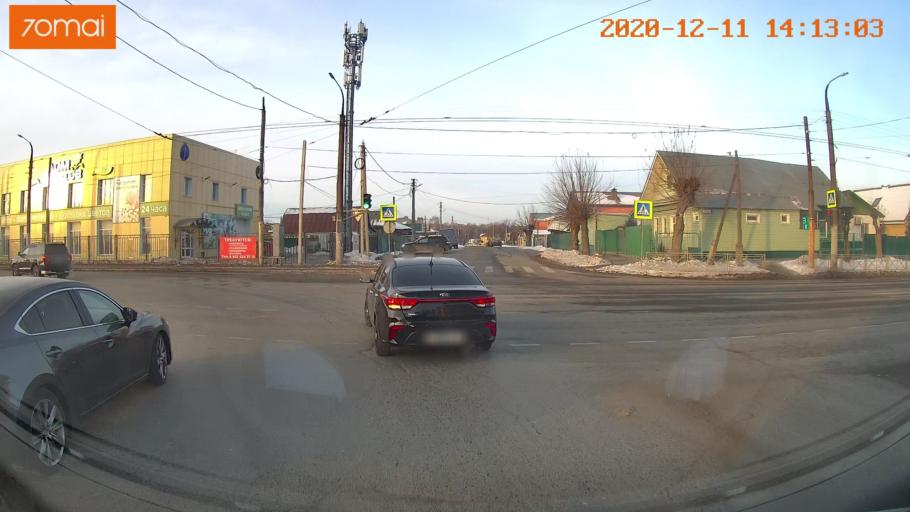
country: RU
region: Kostroma
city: Oktyabr'skiy
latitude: 57.7462
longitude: 40.9626
